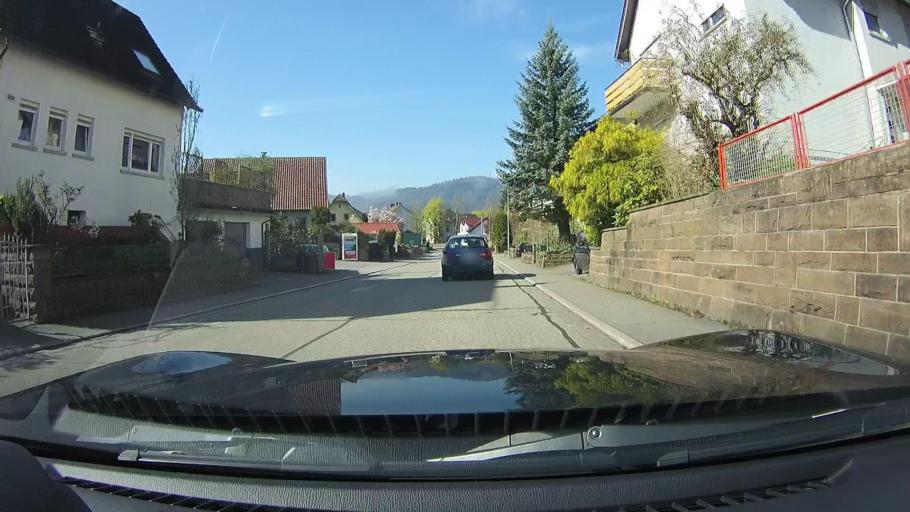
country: DE
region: Baden-Wuerttemberg
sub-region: Karlsruhe Region
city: Eberbach
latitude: 49.4676
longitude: 8.9917
